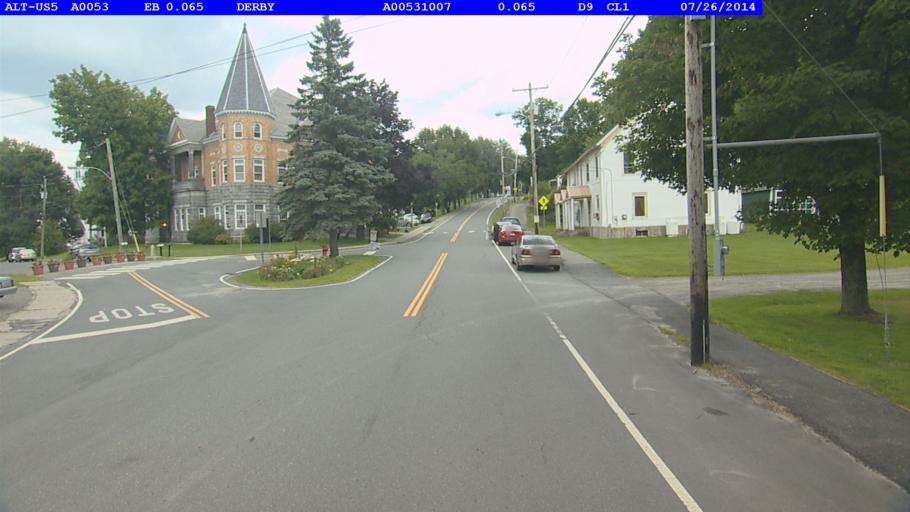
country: US
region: Vermont
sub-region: Orleans County
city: Newport
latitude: 45.0055
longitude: -72.0985
